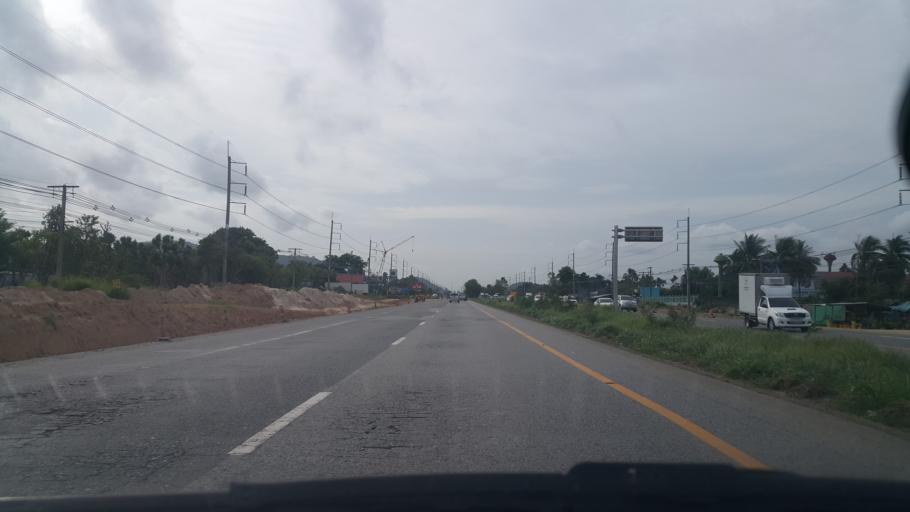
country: TH
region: Rayong
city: Nikhom Phattana
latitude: 12.7997
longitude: 101.1487
